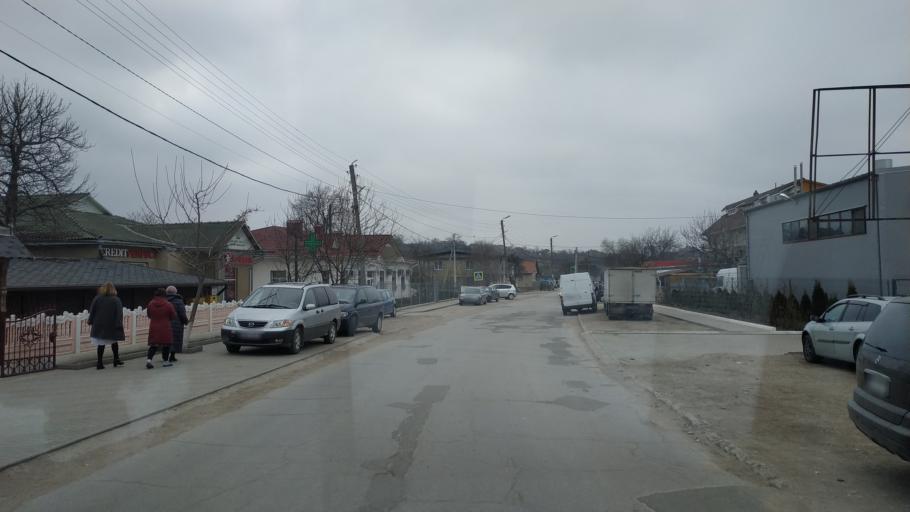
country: MD
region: Hincesti
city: Hincesti
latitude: 46.8819
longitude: 28.4115
